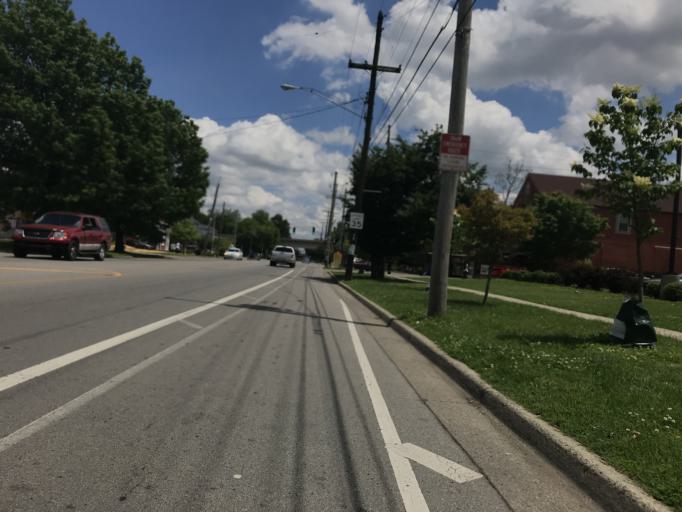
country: US
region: Indiana
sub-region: Floyd County
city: New Albany
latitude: 38.2499
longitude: -85.8096
